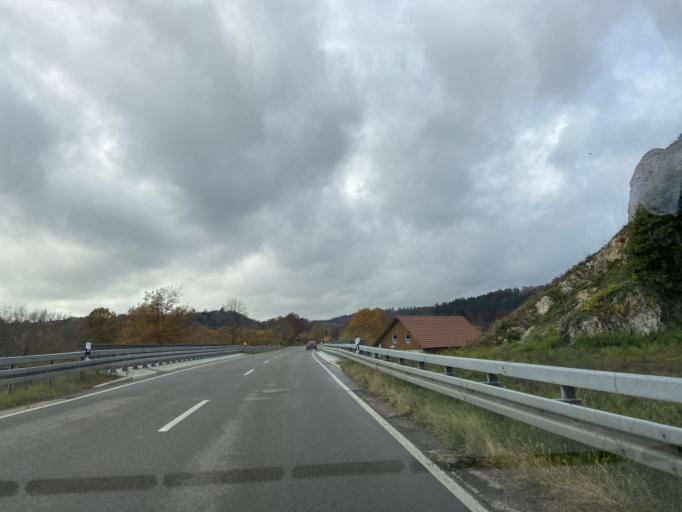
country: DE
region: Baden-Wuerttemberg
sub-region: Tuebingen Region
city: Inzigkofen
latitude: 48.0794
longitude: 9.1918
